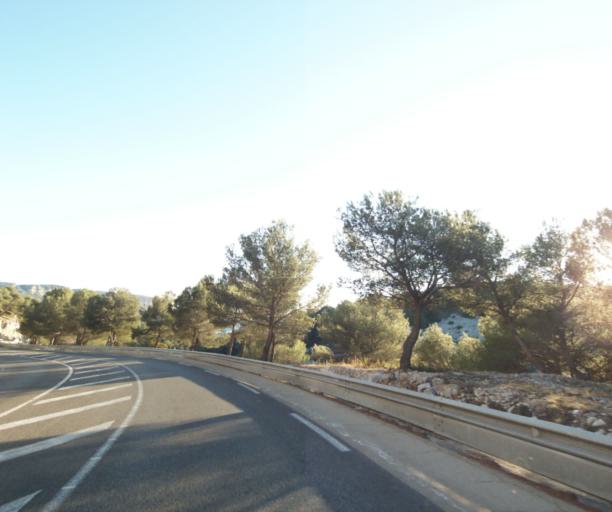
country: FR
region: Provence-Alpes-Cote d'Azur
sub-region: Departement des Bouches-du-Rhone
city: Carnoux-en-Provence
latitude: 43.2412
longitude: 5.5428
